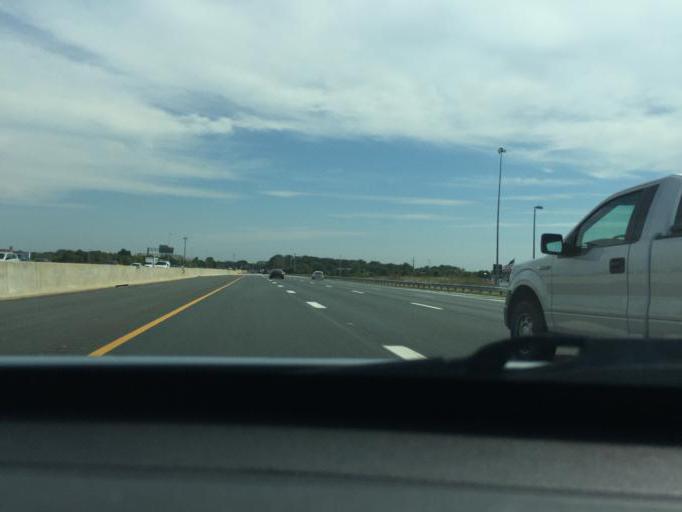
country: US
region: Virginia
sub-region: Prince William County
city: Bull Run
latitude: 38.8013
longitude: -77.5219
